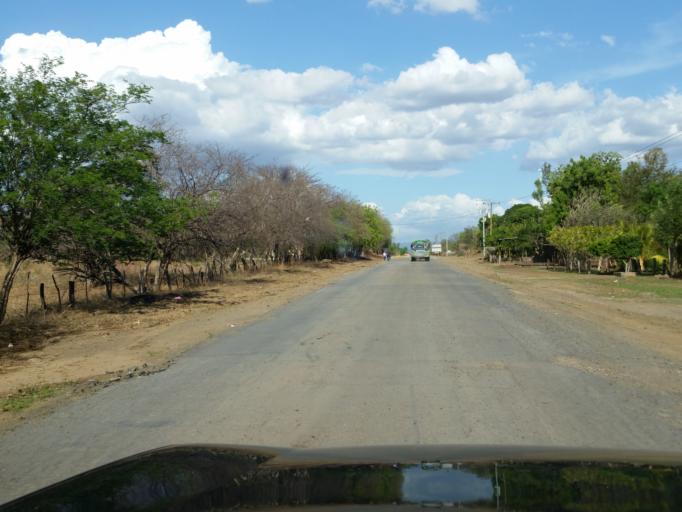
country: NI
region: Managua
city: Carlos Fonseca Amador
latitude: 12.1038
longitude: -86.5800
